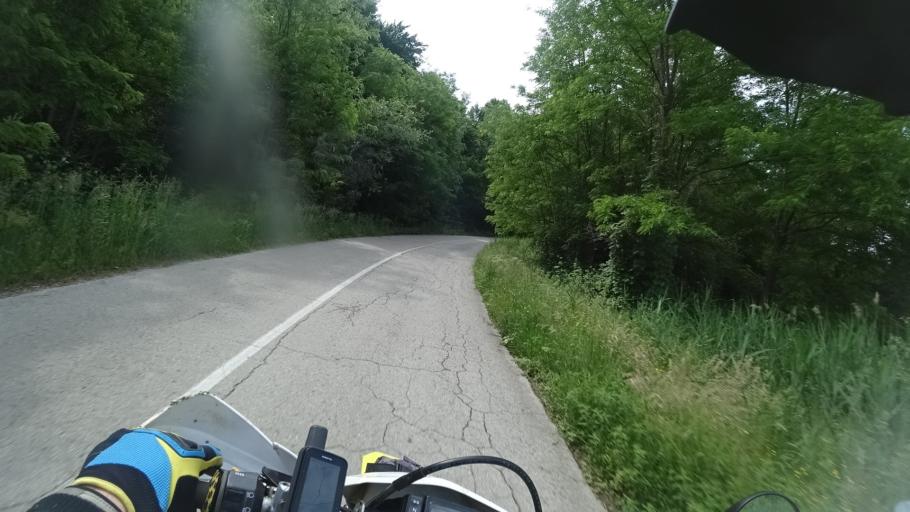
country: HR
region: Sisacko-Moslavacka
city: Gvozd
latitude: 45.3408
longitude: 15.8597
